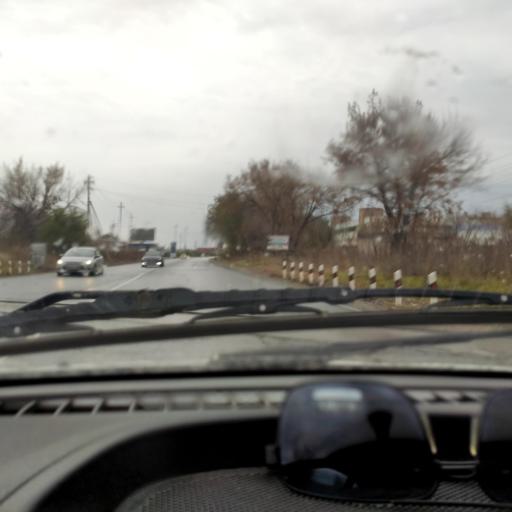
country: RU
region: Samara
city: Tol'yatti
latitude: 53.5298
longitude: 49.4680
